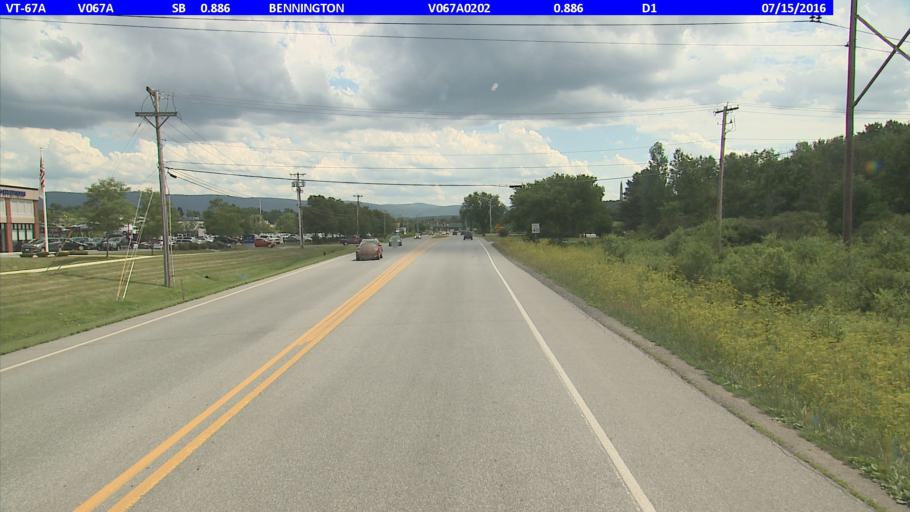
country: US
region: Vermont
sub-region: Bennington County
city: North Bennington
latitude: 42.9108
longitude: -73.2224
